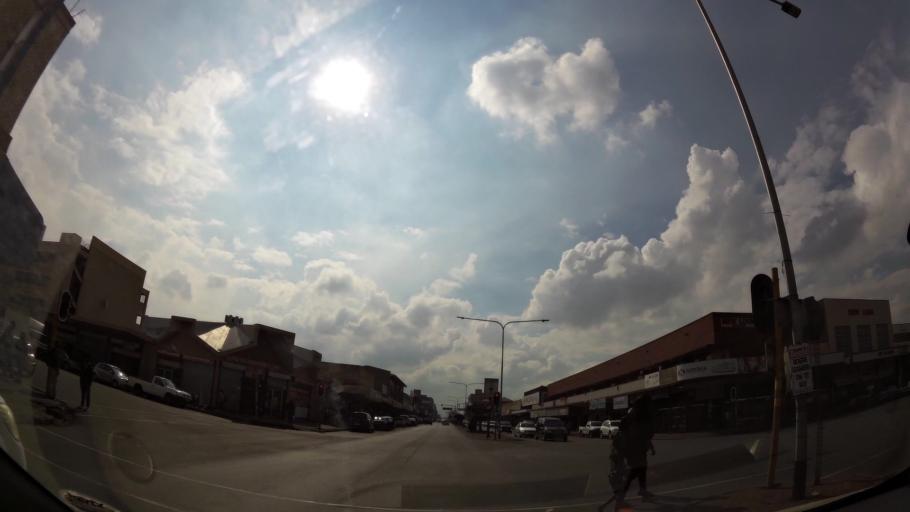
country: ZA
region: Gauteng
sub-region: Sedibeng District Municipality
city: Vereeniging
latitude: -26.6777
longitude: 27.9309
